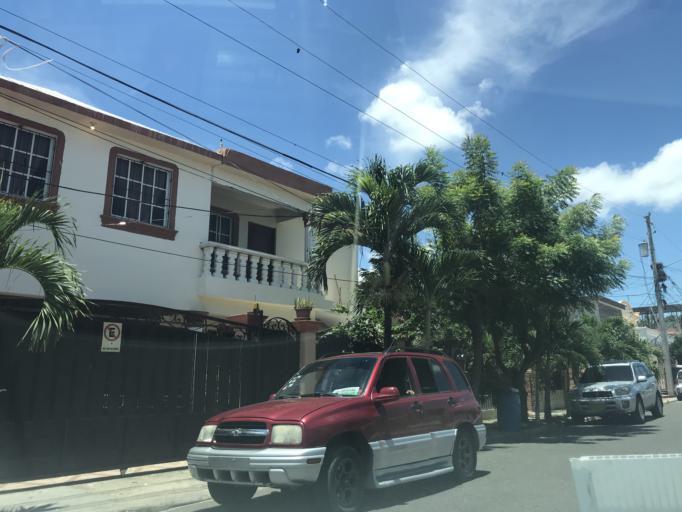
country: DO
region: Santiago
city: Santiago de los Caballeros
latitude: 19.4394
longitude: -70.6942
